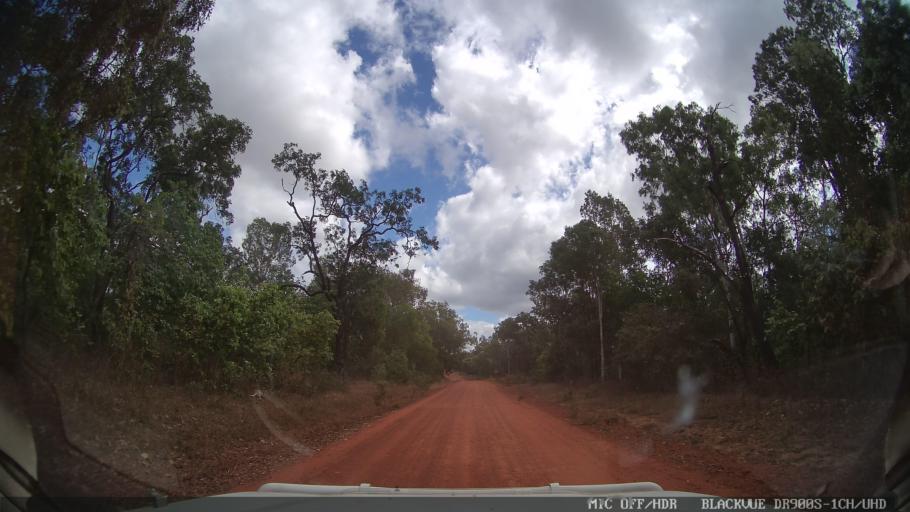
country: AU
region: Queensland
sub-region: Cook
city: Cooktown
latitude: -15.3032
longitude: 144.6118
